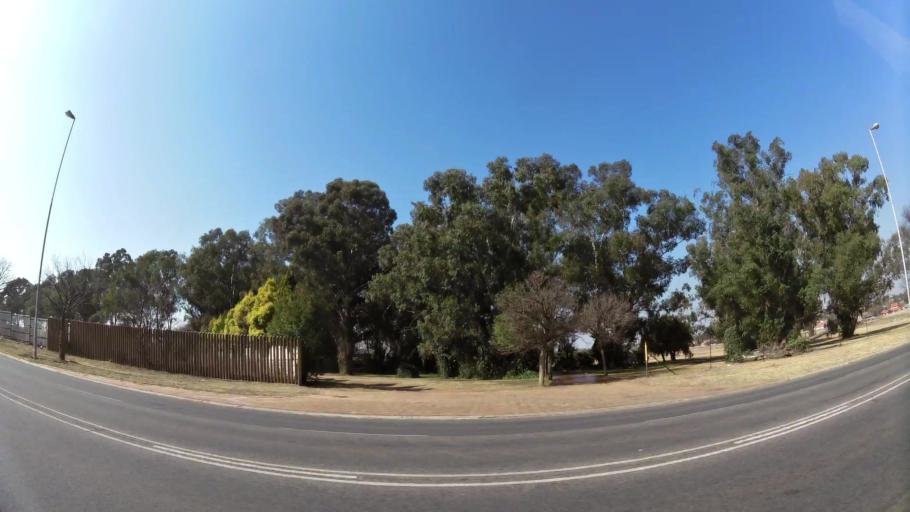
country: ZA
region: Gauteng
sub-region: Ekurhuleni Metropolitan Municipality
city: Boksburg
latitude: -26.2373
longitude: 28.2672
